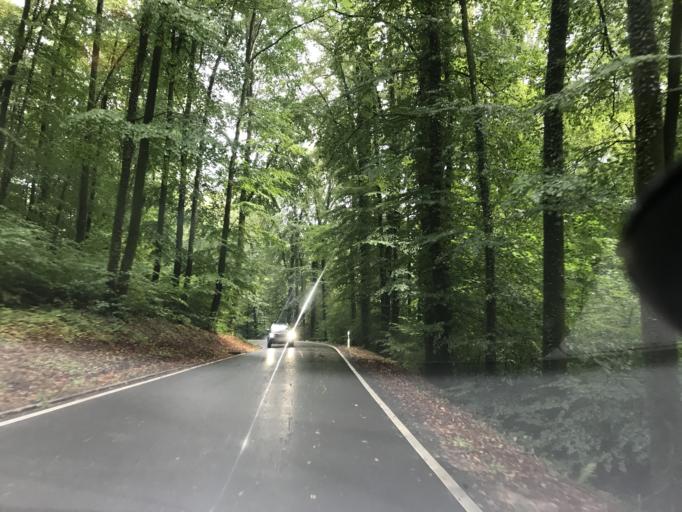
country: DE
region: Baden-Wuerttemberg
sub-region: Freiburg Region
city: Steinen
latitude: 47.6984
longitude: 7.7222
